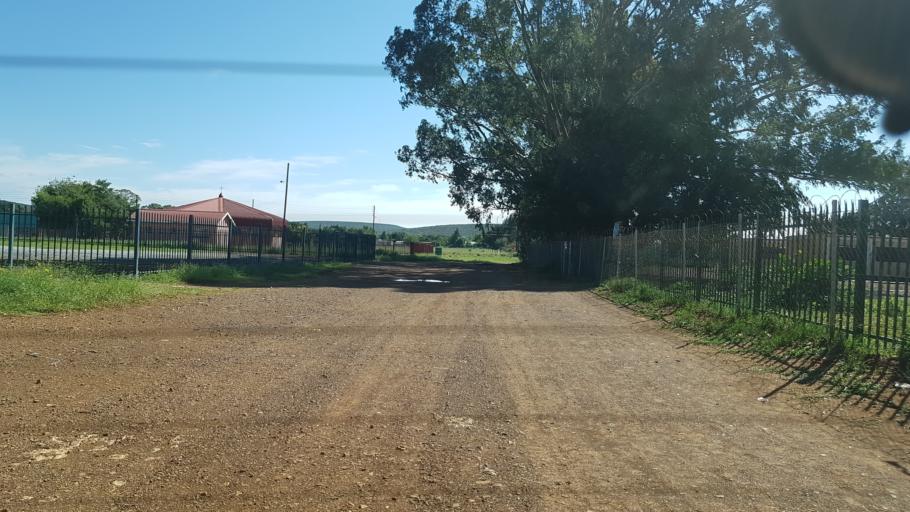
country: ZA
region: Northern Cape
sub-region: Siyanda District Municipality
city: Danielskuil
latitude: -28.1906
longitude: 23.5373
